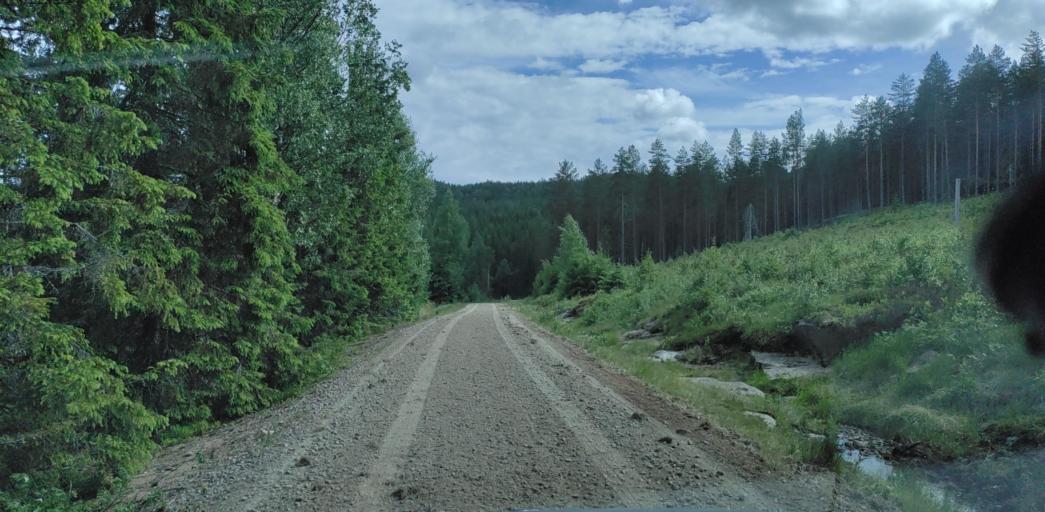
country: SE
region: Vaermland
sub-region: Munkfors Kommun
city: Munkfors
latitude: 59.9673
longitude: 13.4130
